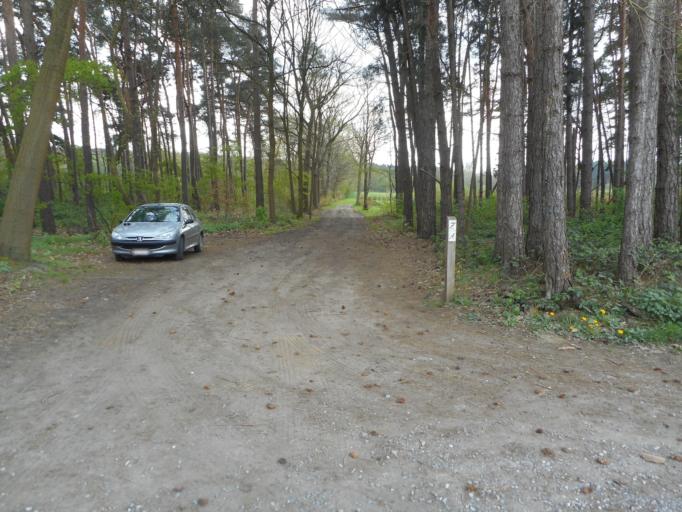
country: BE
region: Flanders
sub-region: Provincie Vlaams-Brabant
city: Aarschot
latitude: 50.9970
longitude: 4.8102
